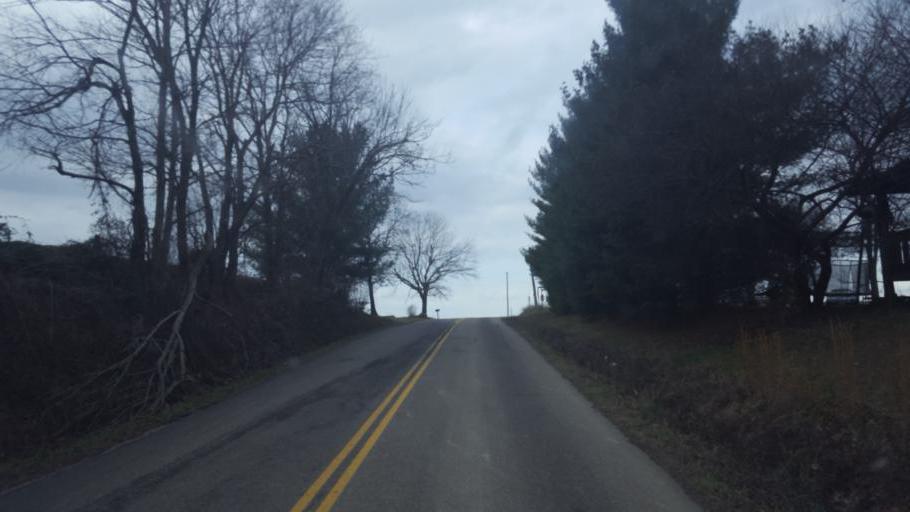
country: US
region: Ohio
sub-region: Gallia County
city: Gallipolis
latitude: 38.7898
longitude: -82.3966
